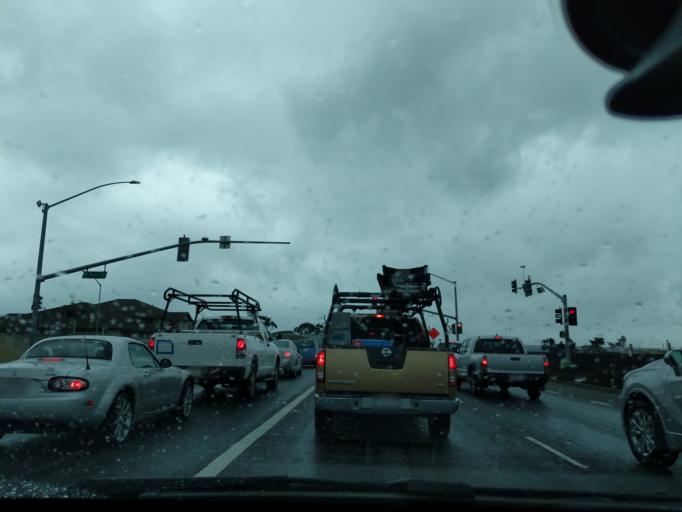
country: US
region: California
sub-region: Monterey County
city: Boronda
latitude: 36.6888
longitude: -121.6716
